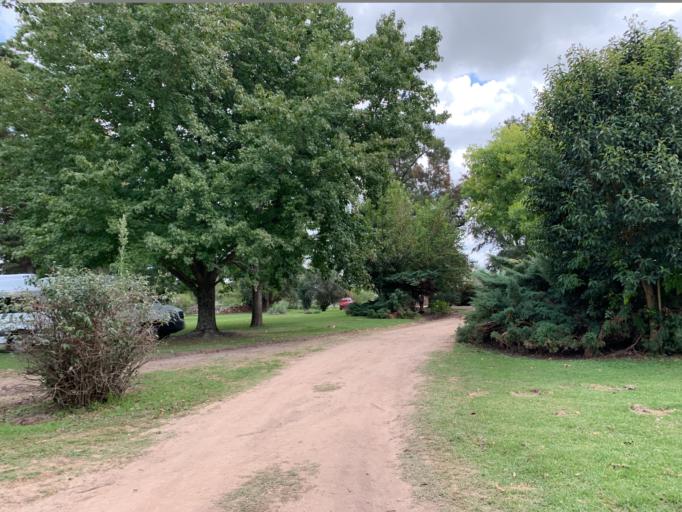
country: AR
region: Buenos Aires
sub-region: San Antonio de Areco
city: San Antonio de Areco
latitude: -34.1969
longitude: -59.3880
